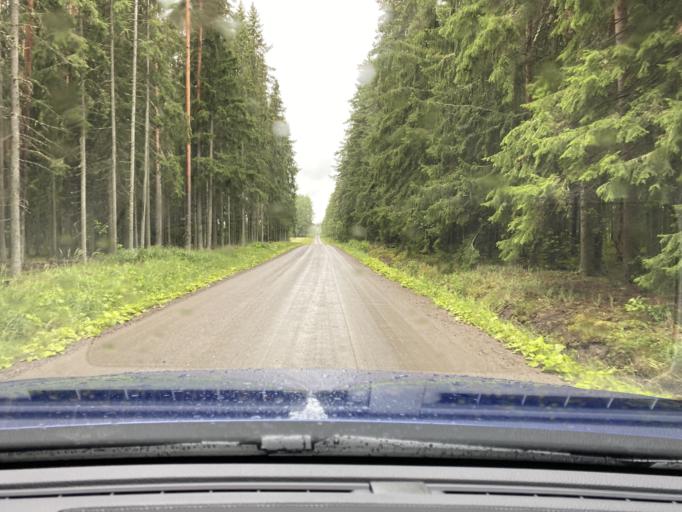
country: FI
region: Pirkanmaa
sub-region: Lounais-Pirkanmaa
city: Punkalaidun
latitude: 61.1482
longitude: 23.2408
